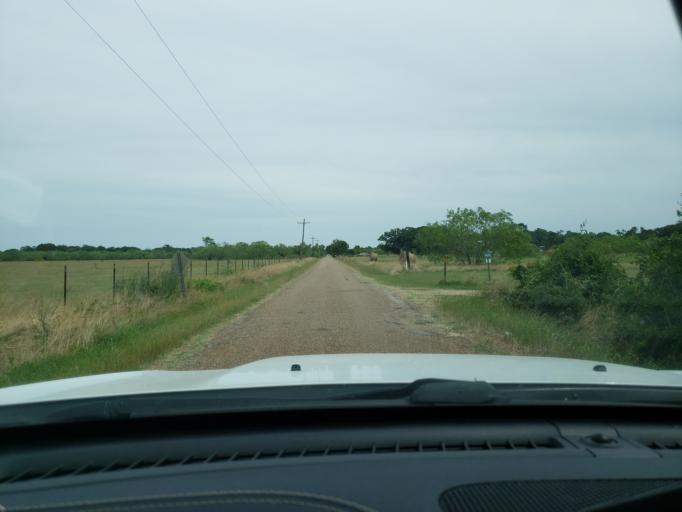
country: US
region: Texas
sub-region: Burleson County
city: Somerville
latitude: 30.3566
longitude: -96.5495
